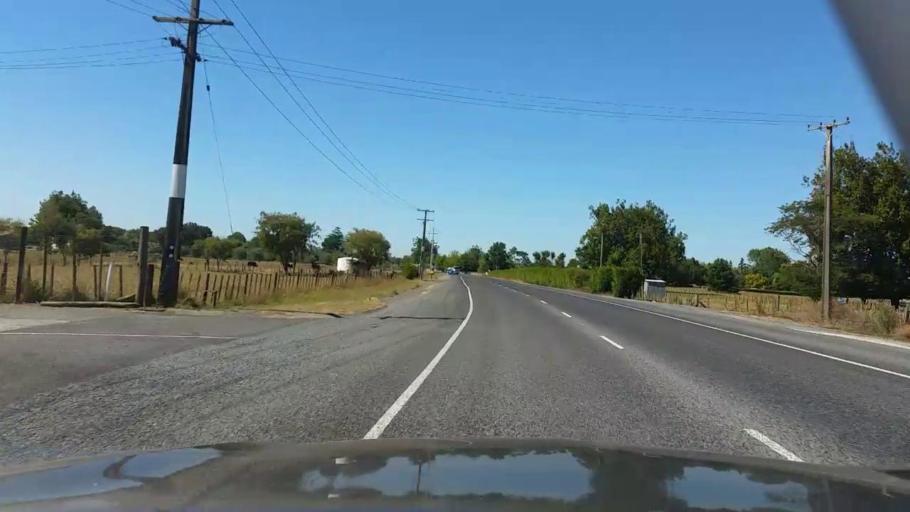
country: NZ
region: Waikato
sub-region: Hamilton City
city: Hamilton
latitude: -37.6656
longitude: 175.2994
